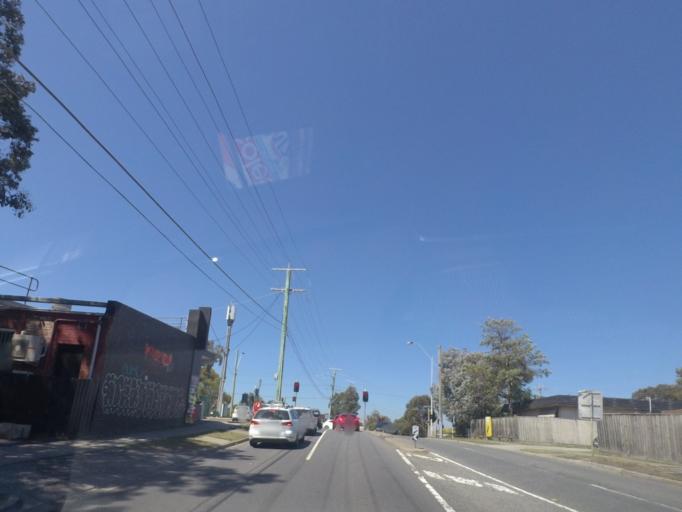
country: AU
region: Victoria
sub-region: Banyule
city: Montmorency
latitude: -37.7098
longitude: 145.1196
